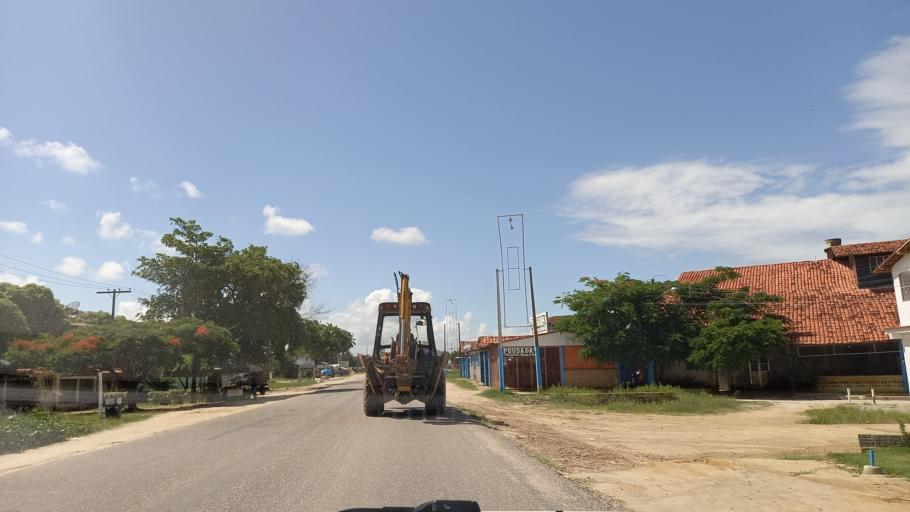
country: BR
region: Pernambuco
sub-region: Sao Jose Da Coroa Grande
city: Sao Jose da Coroa Grande
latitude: -8.8992
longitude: -35.1509
